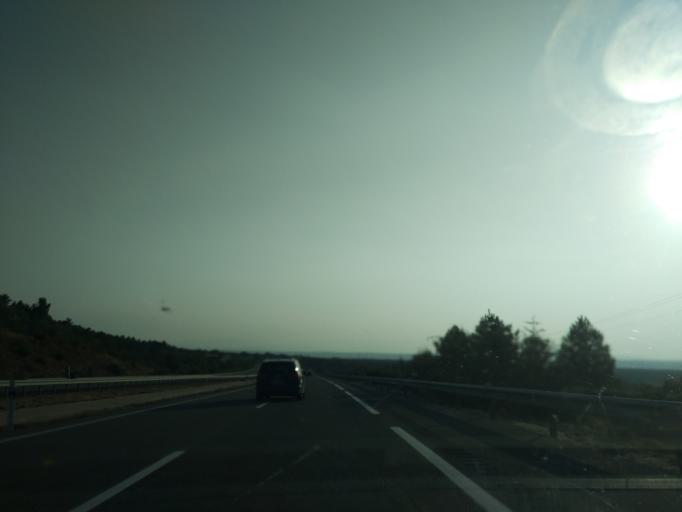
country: ES
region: Castille and Leon
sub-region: Provincia de Avila
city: Ojos-Albos
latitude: 40.7340
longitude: -4.5031
